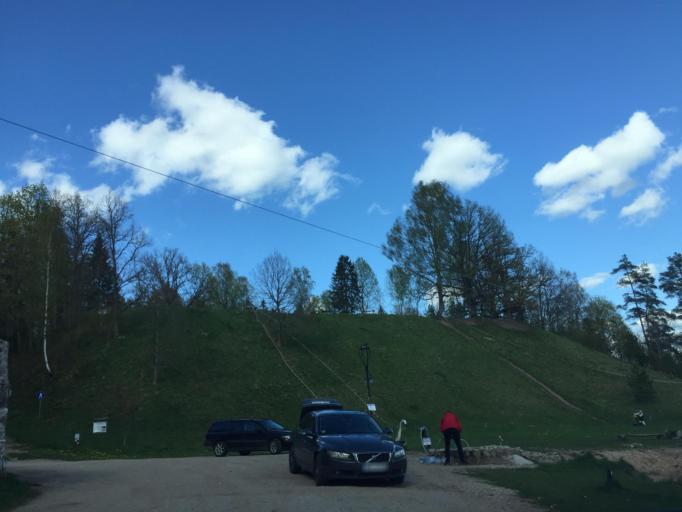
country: LV
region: Madonas Rajons
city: Madona
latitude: 56.8098
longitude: 26.0949
